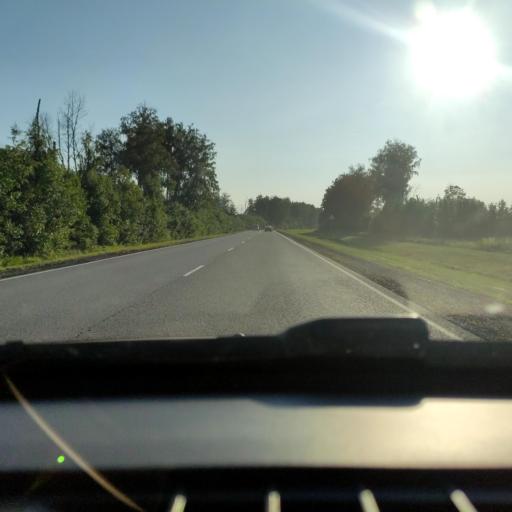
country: RU
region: Voronezj
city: Kashirskoye
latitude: 51.4585
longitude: 39.7717
